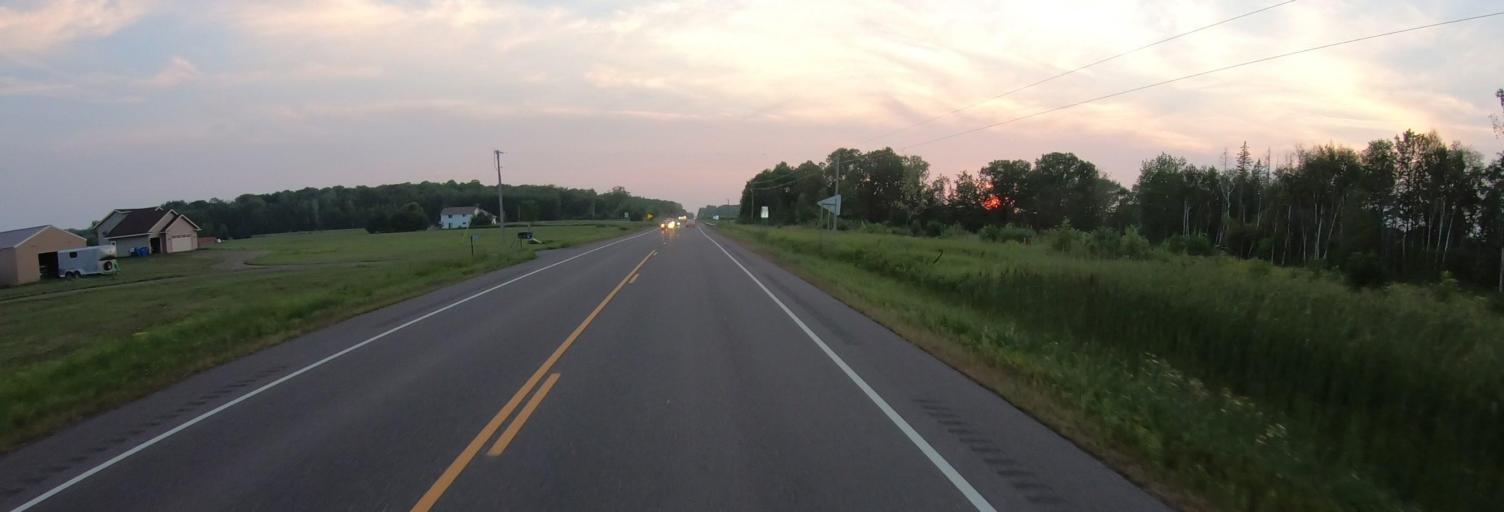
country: US
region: Minnesota
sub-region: Pine County
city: Rock Creek
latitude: 45.7735
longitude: -92.8533
